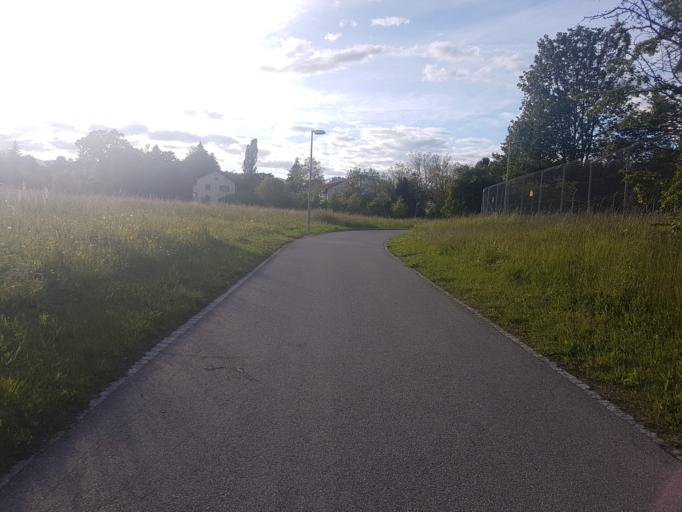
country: CH
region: Geneva
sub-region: Geneva
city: Vernier
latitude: 46.2166
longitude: 6.0957
